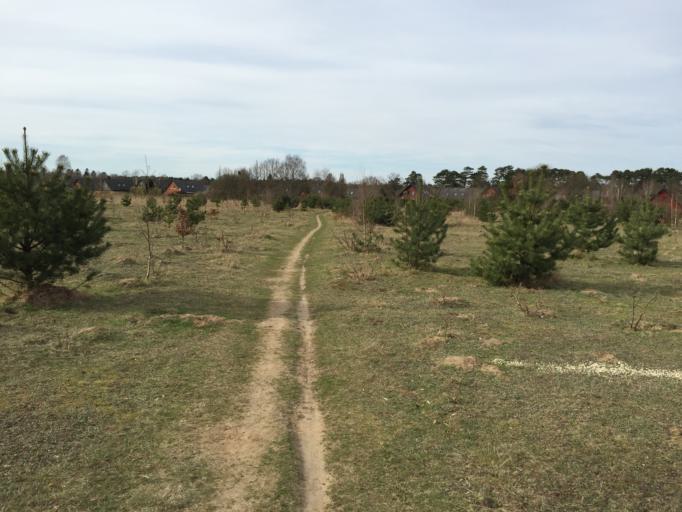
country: SE
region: Skane
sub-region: Lunds Kommun
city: Veberod
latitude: 55.6270
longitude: 13.5101
